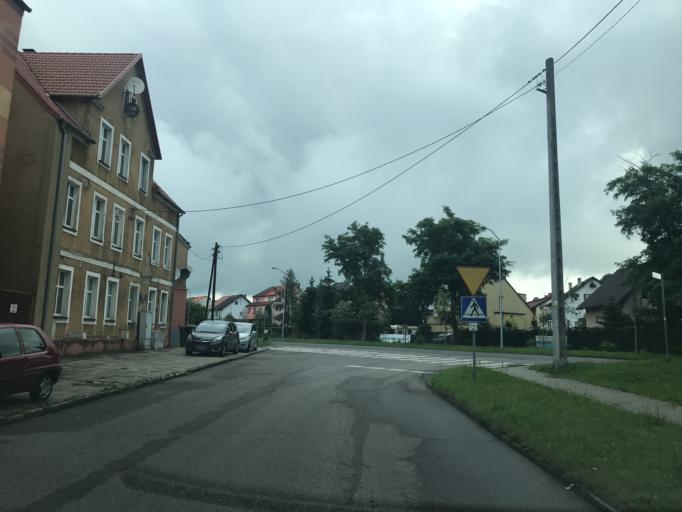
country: PL
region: West Pomeranian Voivodeship
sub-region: Powiat goleniowski
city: Goleniow
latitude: 53.5715
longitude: 14.8310
